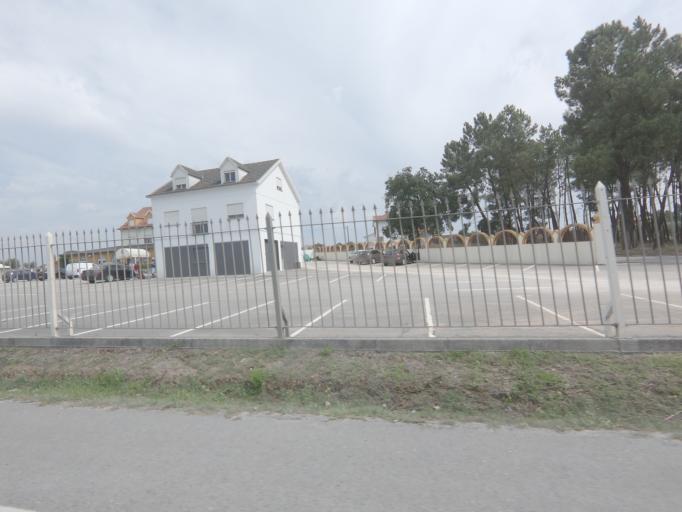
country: PT
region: Leiria
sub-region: Pombal
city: Pombal
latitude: 39.8721
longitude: -8.6900
